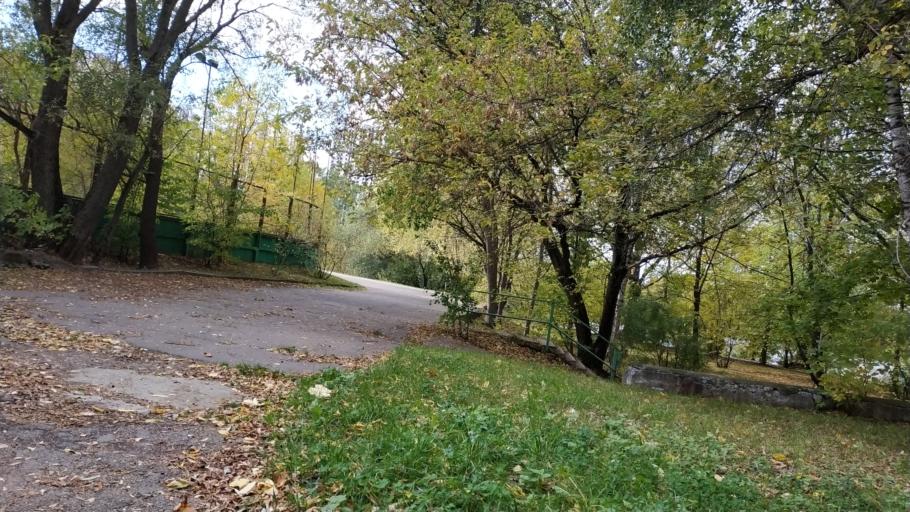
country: RU
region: Moscow
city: Metrogorodok
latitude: 55.7920
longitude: 37.7563
